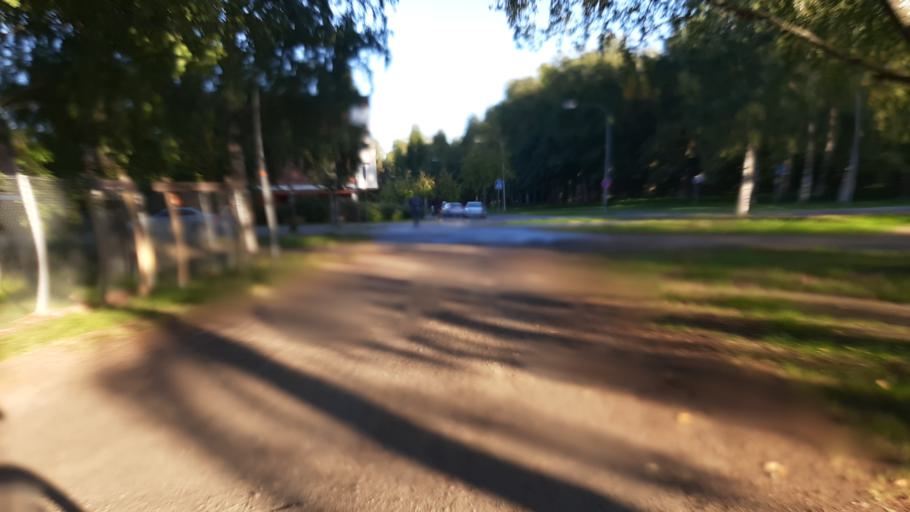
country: FI
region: North Karelia
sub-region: Joensuu
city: Joensuu
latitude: 62.5949
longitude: 29.7409
